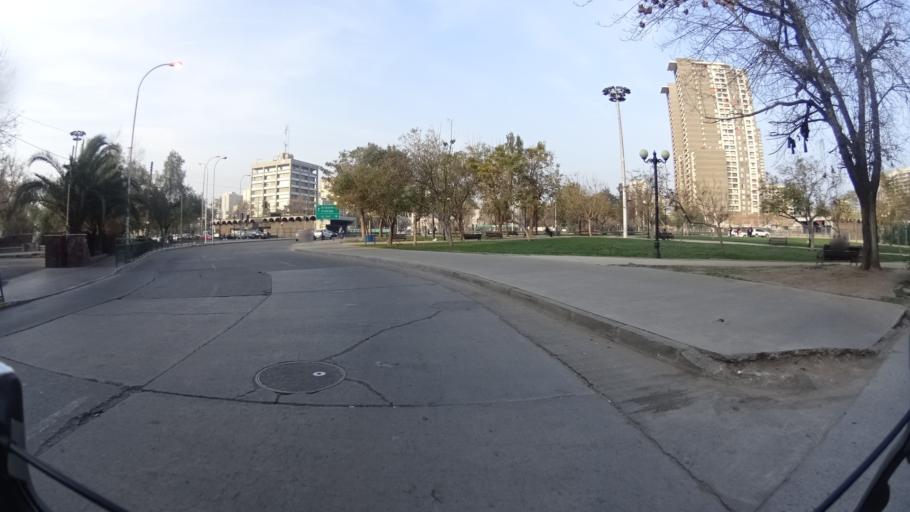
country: CL
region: Santiago Metropolitan
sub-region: Provincia de Santiago
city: Santiago
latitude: -33.4530
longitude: -70.6597
